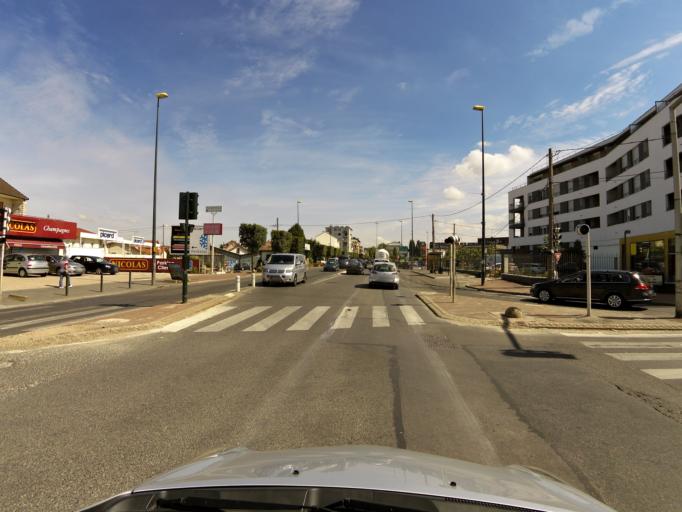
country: FR
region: Ile-de-France
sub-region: Departement de Seine-Saint-Denis
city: Gournay-sur-Marne
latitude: 48.8688
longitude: 2.5737
